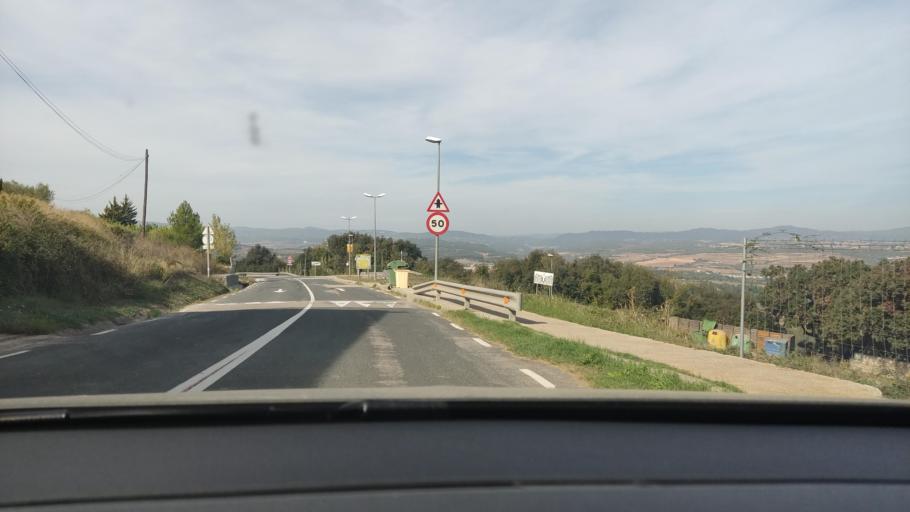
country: ES
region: Catalonia
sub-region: Provincia de Barcelona
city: Sant Sadurni d'Anoia
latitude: 41.4091
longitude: 1.8085
